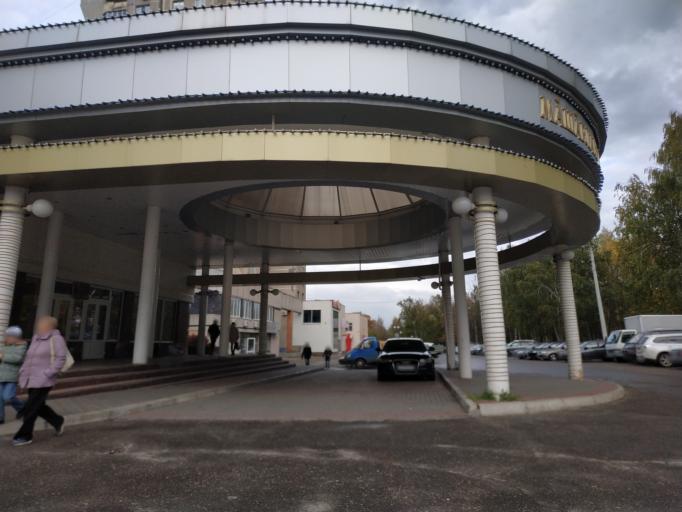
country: RU
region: Chuvashia
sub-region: Cheboksarskiy Rayon
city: Cheboksary
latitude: 56.1462
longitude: 47.2164
